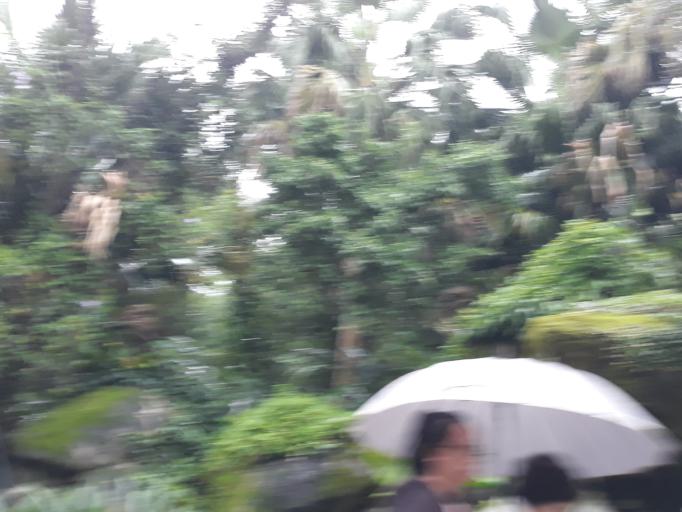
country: TW
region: Taipei
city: Taipei
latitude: 24.9953
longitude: 121.5861
